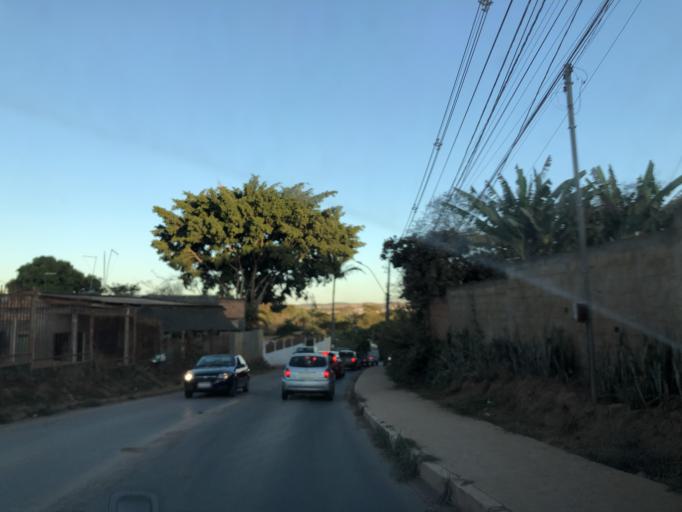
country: BR
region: Federal District
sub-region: Brasilia
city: Brasilia
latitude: -15.8794
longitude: -47.7788
